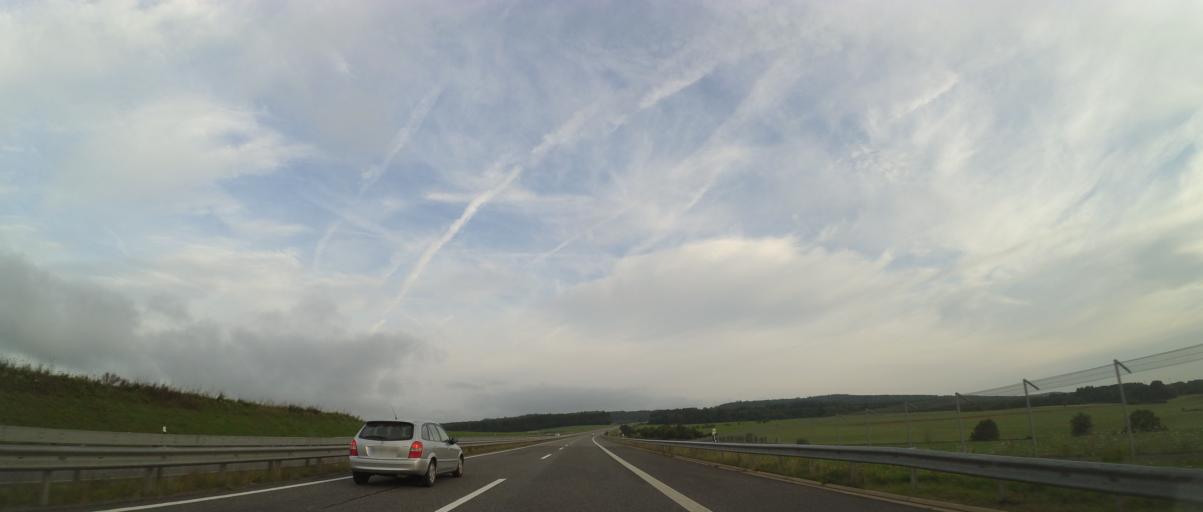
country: DE
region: Rheinland-Pfalz
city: Kradenbach
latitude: 50.2342
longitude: 6.8424
